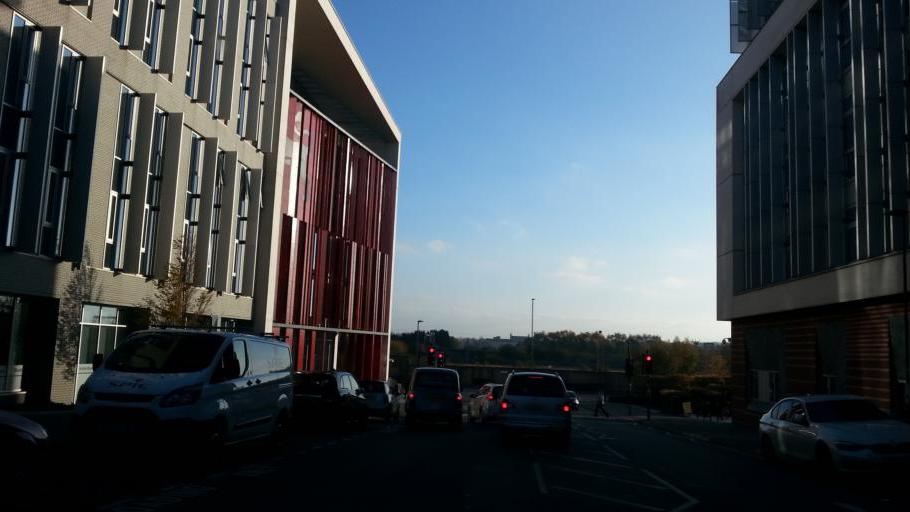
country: GB
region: England
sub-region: City and Borough of Birmingham
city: Birmingham
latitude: 52.4833
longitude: -1.8837
